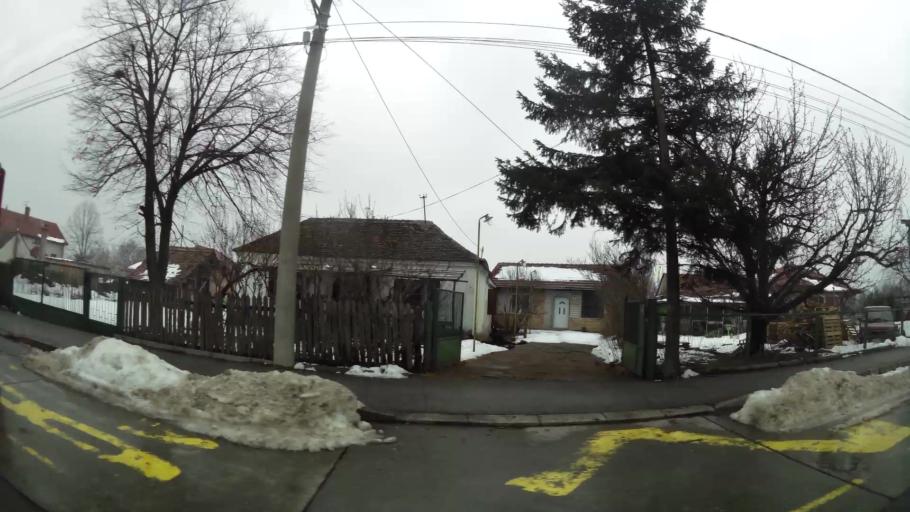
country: RS
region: Central Serbia
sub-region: Belgrade
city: Vozdovac
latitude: 44.7534
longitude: 20.4918
